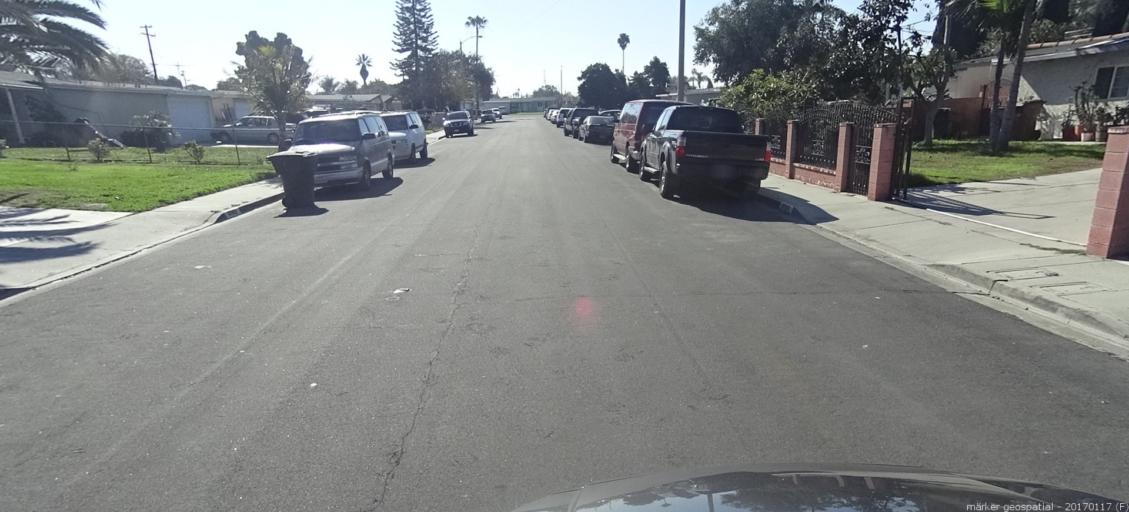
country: US
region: California
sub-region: Orange County
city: Stanton
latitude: 33.8157
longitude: -117.9608
